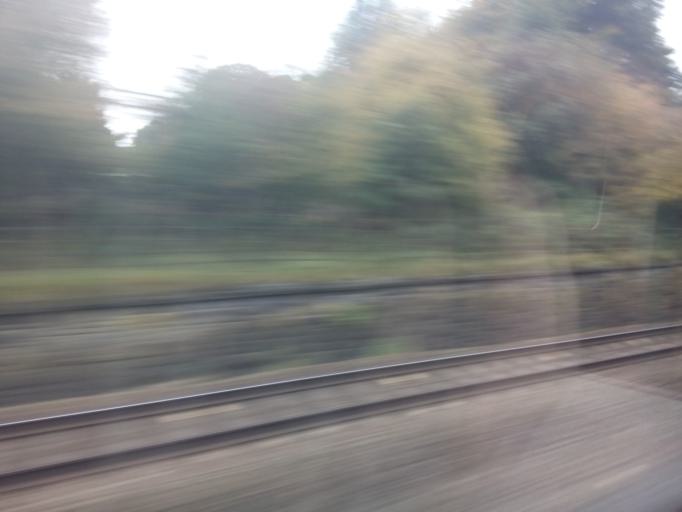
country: GB
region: England
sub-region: Kirklees
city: Mirfield
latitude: 53.6714
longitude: -1.6713
